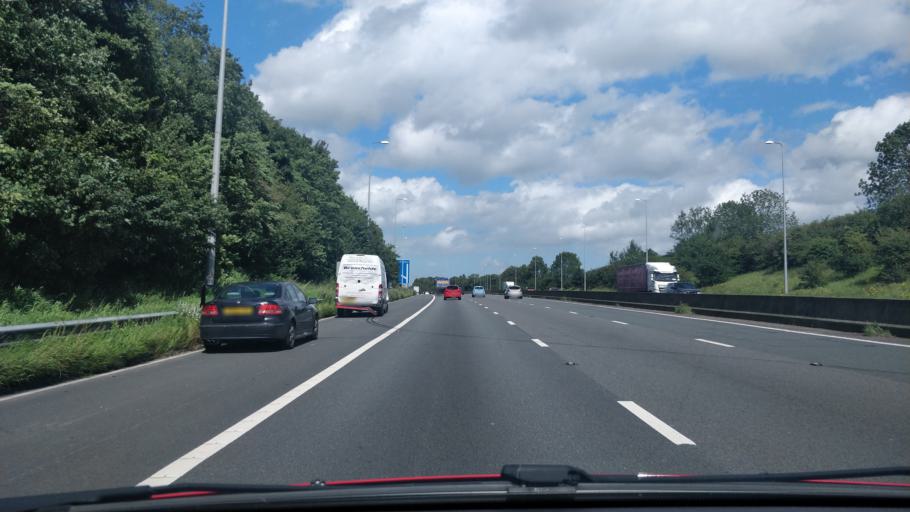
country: GB
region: England
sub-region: Borough of Wigan
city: Shevington
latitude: 53.5832
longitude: -2.6940
